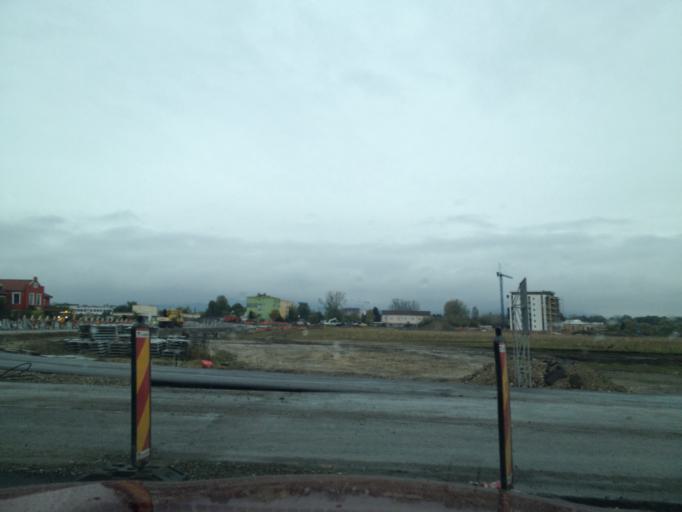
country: RO
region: Brasov
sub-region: Comuna Sanpetru
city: Sanpetru
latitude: 45.6898
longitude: 25.6197
